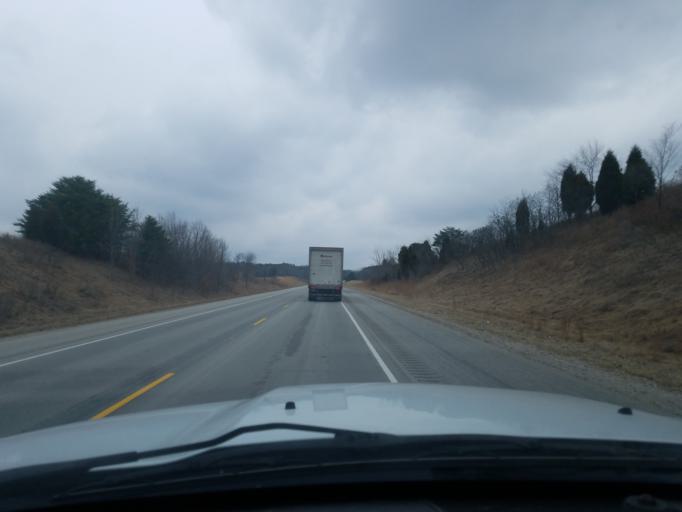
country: US
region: Indiana
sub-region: Perry County
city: Tell City
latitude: 38.0943
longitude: -86.6125
